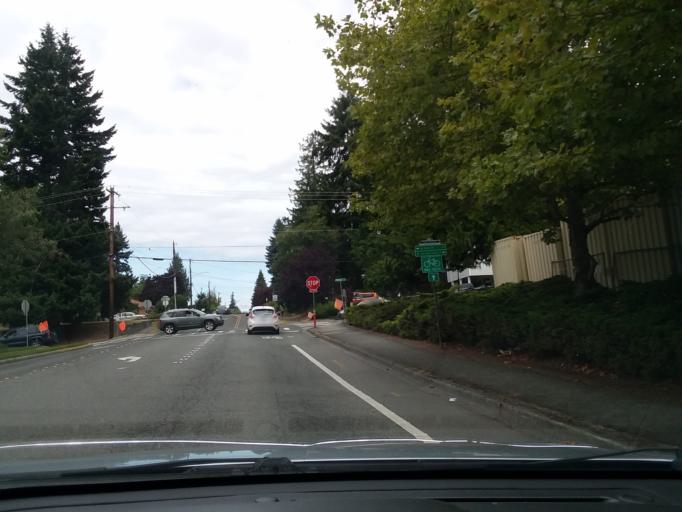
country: US
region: Washington
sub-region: Snohomish County
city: Alderwood Manor
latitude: 47.8225
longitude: -122.2978
